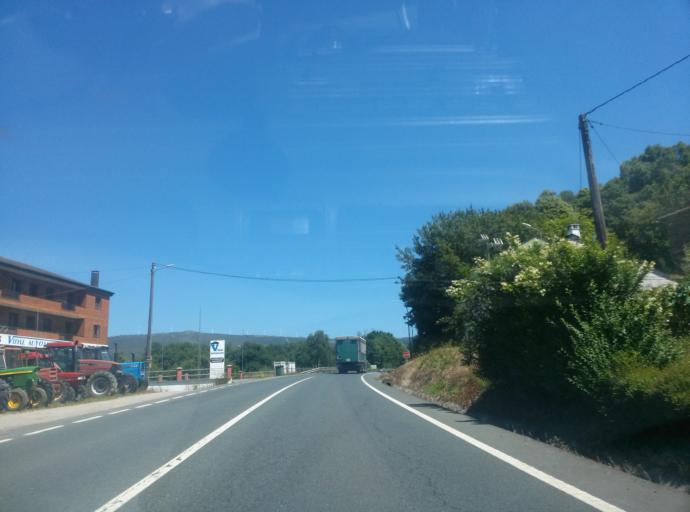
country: ES
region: Galicia
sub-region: Provincia de Lugo
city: Meira
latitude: 43.2153
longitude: -7.3042
